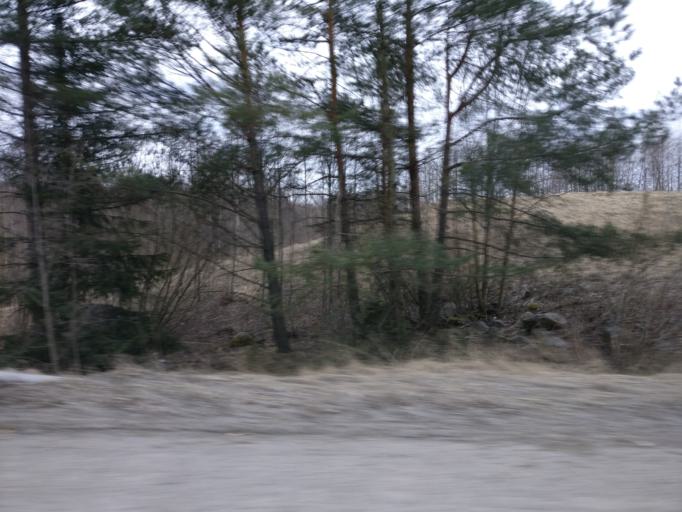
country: FI
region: Pirkanmaa
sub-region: Tampere
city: Tampere
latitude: 61.4747
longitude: 23.8367
